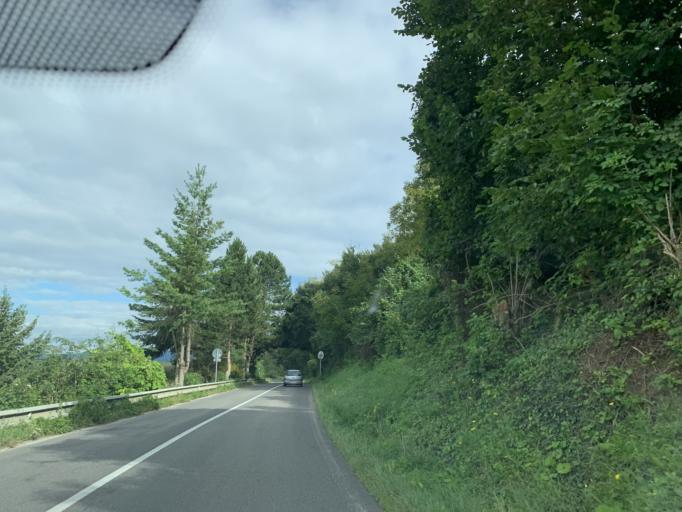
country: SK
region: Trenciansky
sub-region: Okres Trencin
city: Trencin
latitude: 48.8277
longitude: 17.9536
